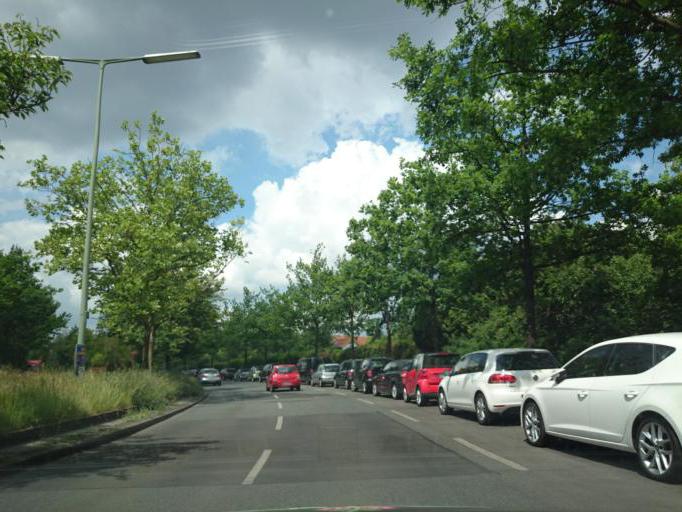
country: DE
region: Berlin
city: Schoneberg Bezirk
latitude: 52.4592
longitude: 13.3542
